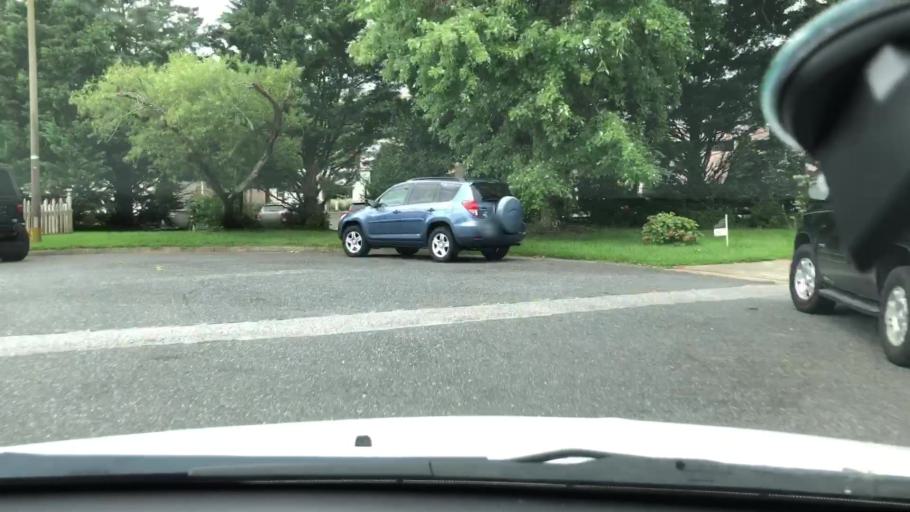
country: US
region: Virginia
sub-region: City of Virginia Beach
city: Virginia Beach
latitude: 36.8451
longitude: -76.1180
